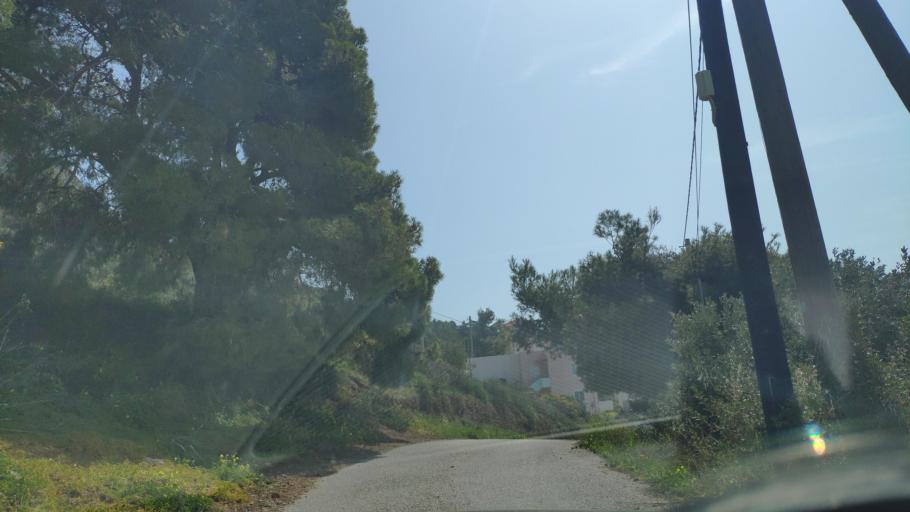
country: GR
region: Attica
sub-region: Nomarchia Anatolikis Attikis
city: Limin Mesoyaias
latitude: 37.9018
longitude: 24.0297
